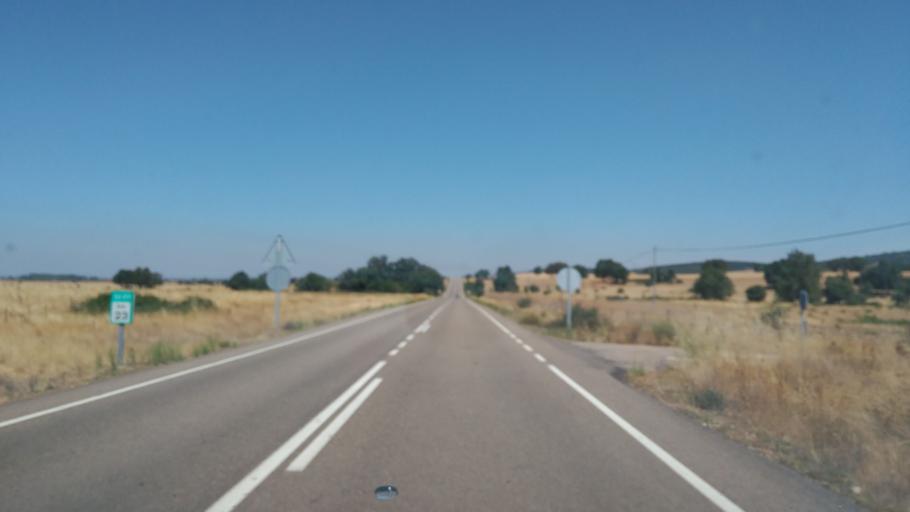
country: ES
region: Castille and Leon
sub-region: Provincia de Salamanca
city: Aldeanueva de la Sierra
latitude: 40.6293
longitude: -6.1080
